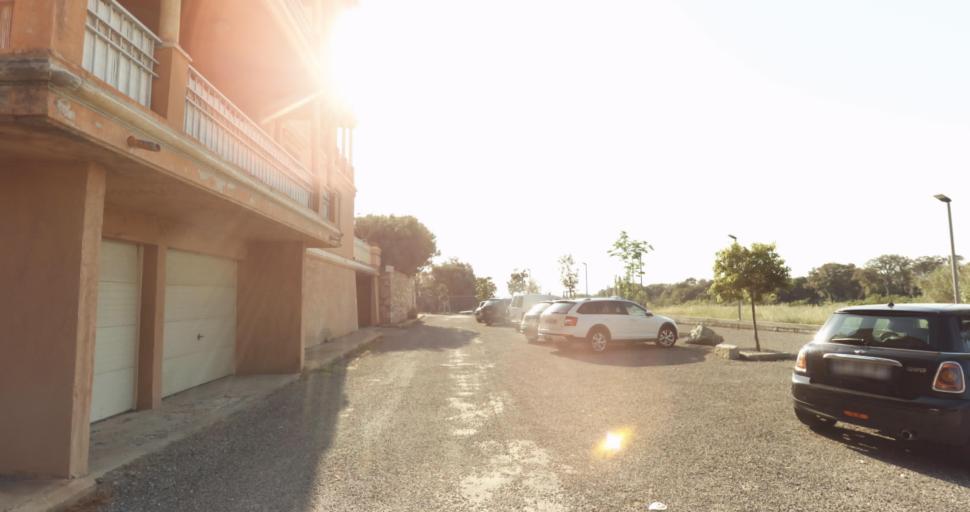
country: FR
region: Corsica
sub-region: Departement de la Haute-Corse
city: Biguglia
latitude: 42.6258
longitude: 9.4381
